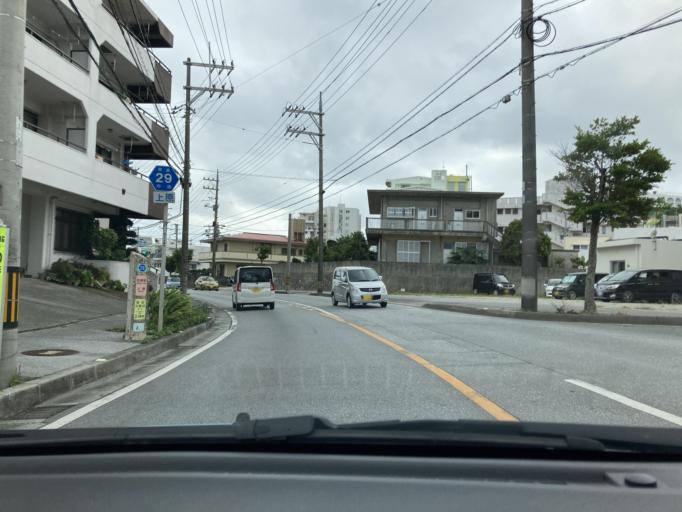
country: JP
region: Okinawa
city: Ginowan
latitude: 26.2411
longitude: 127.7646
